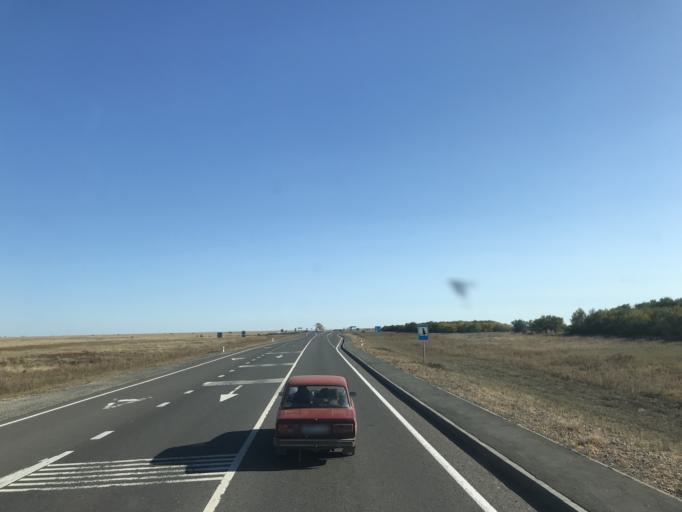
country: KZ
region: Pavlodar
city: Aksu
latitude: 52.0196
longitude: 77.2305
